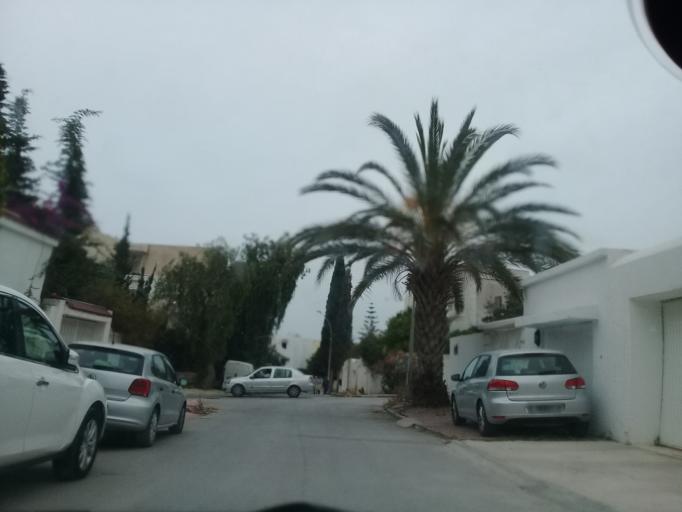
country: TN
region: Tunis
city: Tunis
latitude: 36.8441
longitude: 10.1482
